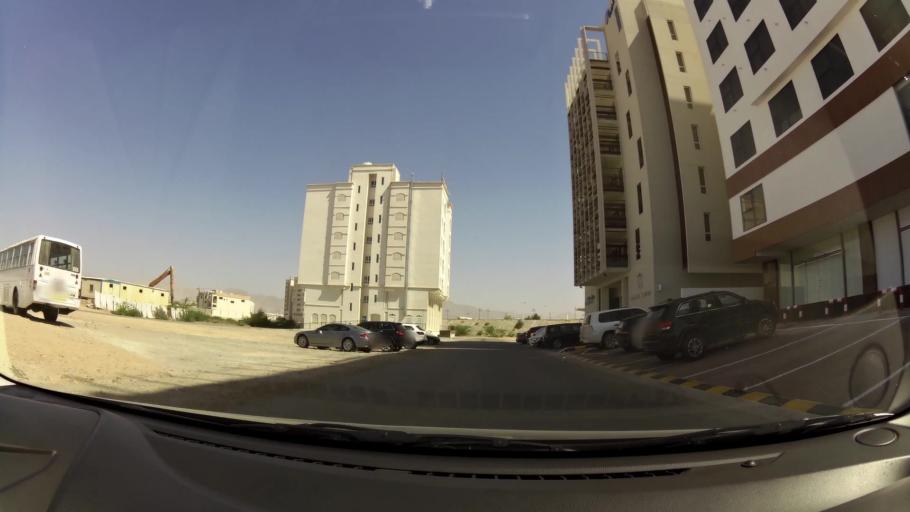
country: OM
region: Muhafazat Masqat
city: Bawshar
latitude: 23.5941
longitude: 58.3498
